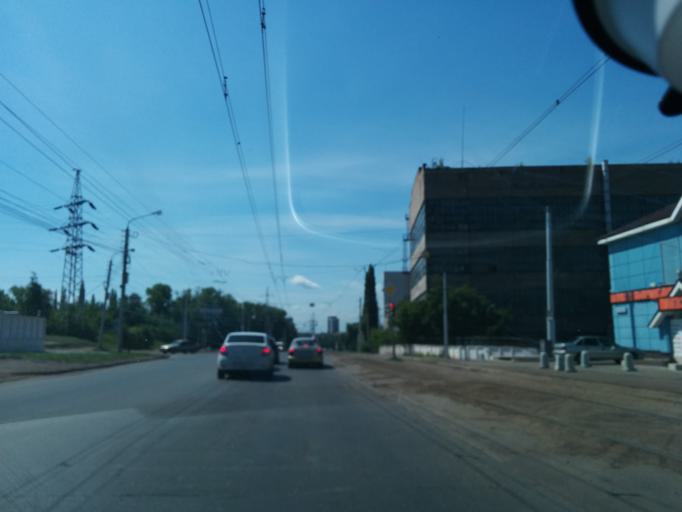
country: RU
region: Bashkortostan
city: Ufa
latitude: 54.7419
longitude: 55.9752
